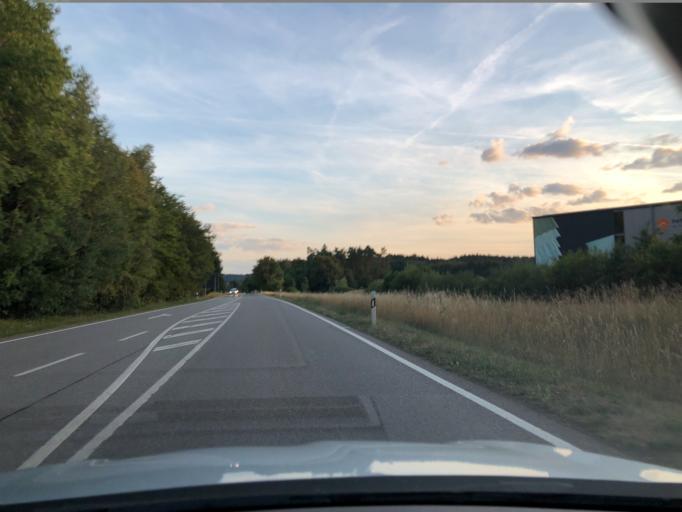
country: DE
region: Bavaria
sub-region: Upper Palatinate
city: Illschwang
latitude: 49.4564
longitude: 11.6736
